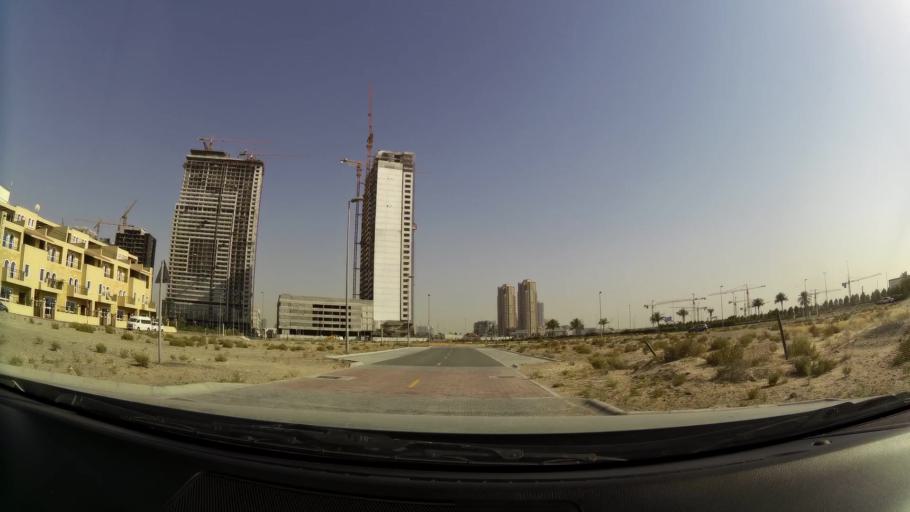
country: AE
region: Dubai
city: Dubai
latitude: 25.0560
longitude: 55.1975
